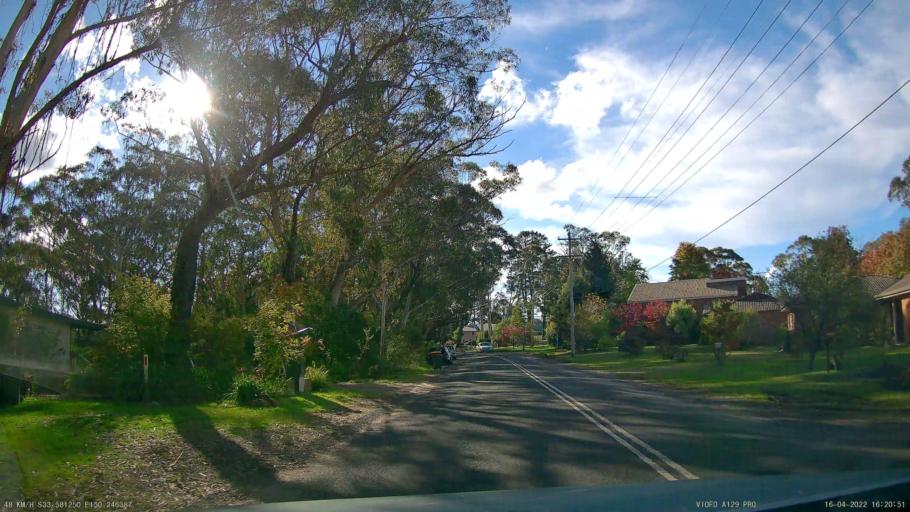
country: AU
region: New South Wales
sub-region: Blue Mountains Municipality
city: Blackheath
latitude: -33.5811
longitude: 150.2463
